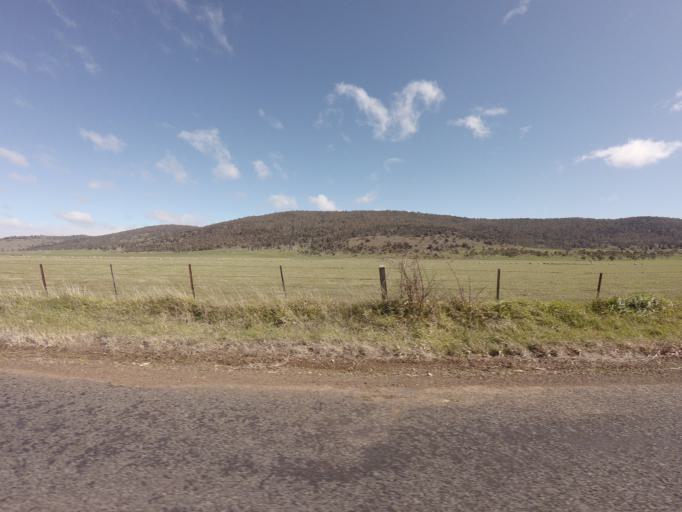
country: AU
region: Tasmania
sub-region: Northern Midlands
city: Evandale
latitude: -41.9709
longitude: 147.4432
